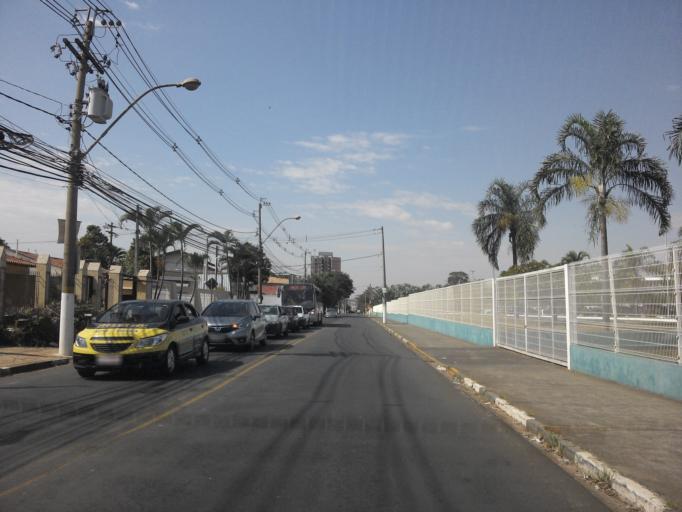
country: BR
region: Sao Paulo
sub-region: Hortolandia
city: Hortolandia
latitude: -22.8751
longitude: -47.2284
